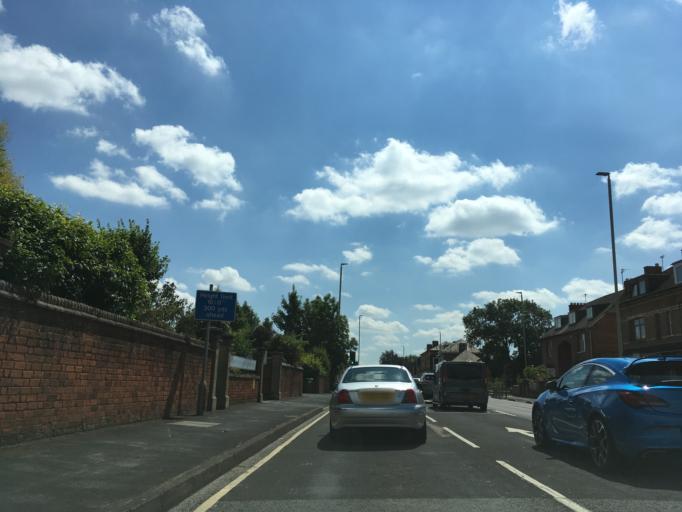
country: GB
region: England
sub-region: Gloucestershire
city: Barnwood
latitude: 51.8661
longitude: -2.2188
